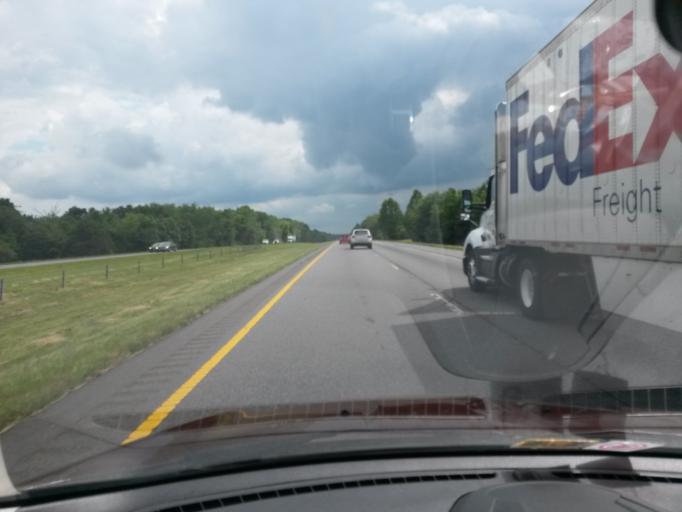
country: US
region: North Carolina
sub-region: Iredell County
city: Statesville
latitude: 35.9584
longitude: -80.8477
